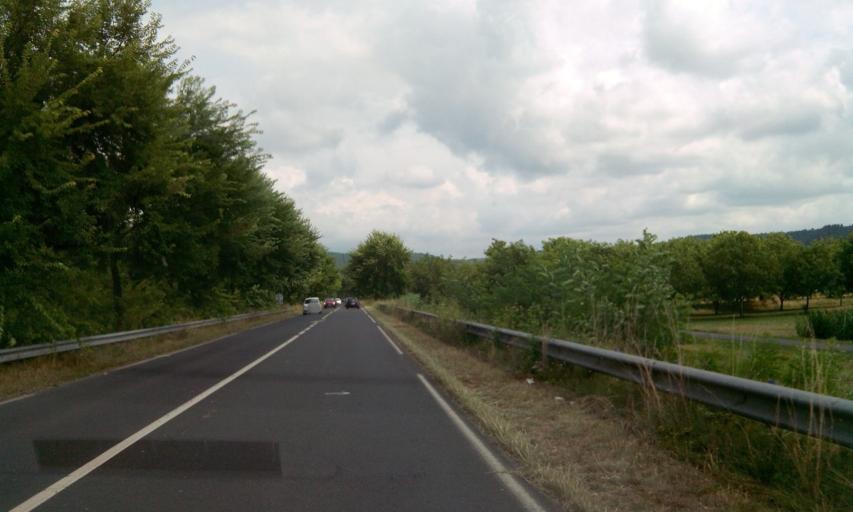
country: FR
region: Midi-Pyrenees
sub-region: Departement du Lot
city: Souillac
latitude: 44.8847
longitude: 1.4105
